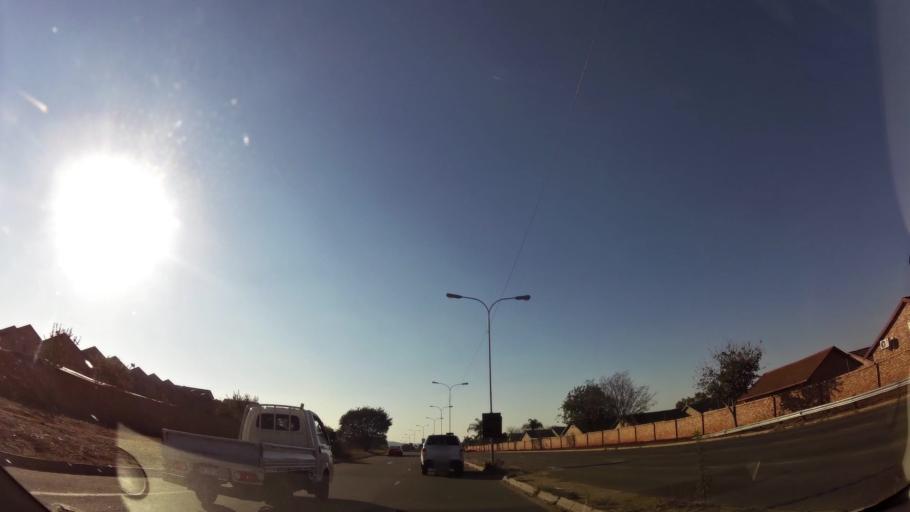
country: ZA
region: Gauteng
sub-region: City of Tshwane Metropolitan Municipality
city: Centurion
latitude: -25.8822
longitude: 28.1413
